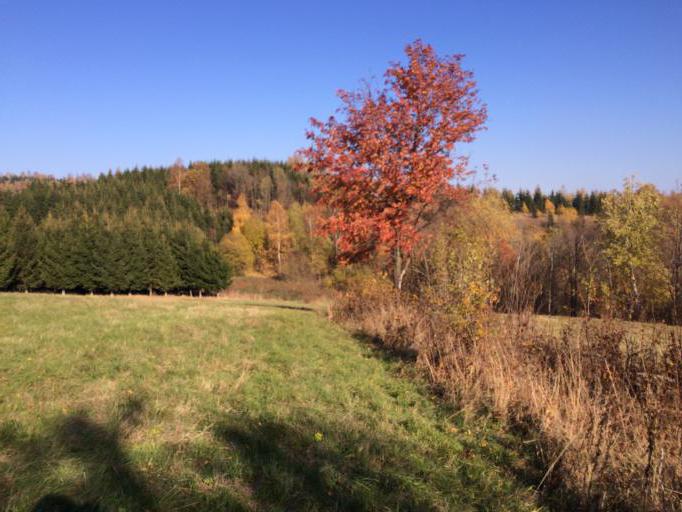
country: PL
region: Lower Silesian Voivodeship
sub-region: Powiat klodzki
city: Miedzylesie
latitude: 50.1970
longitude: 16.6099
